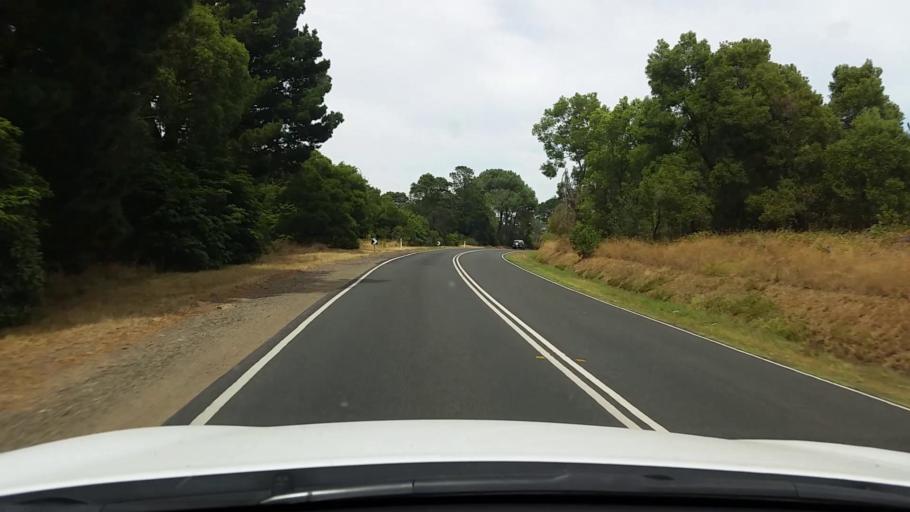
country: AU
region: Victoria
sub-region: Mornington Peninsula
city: Merricks
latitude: -38.3819
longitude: 145.1094
